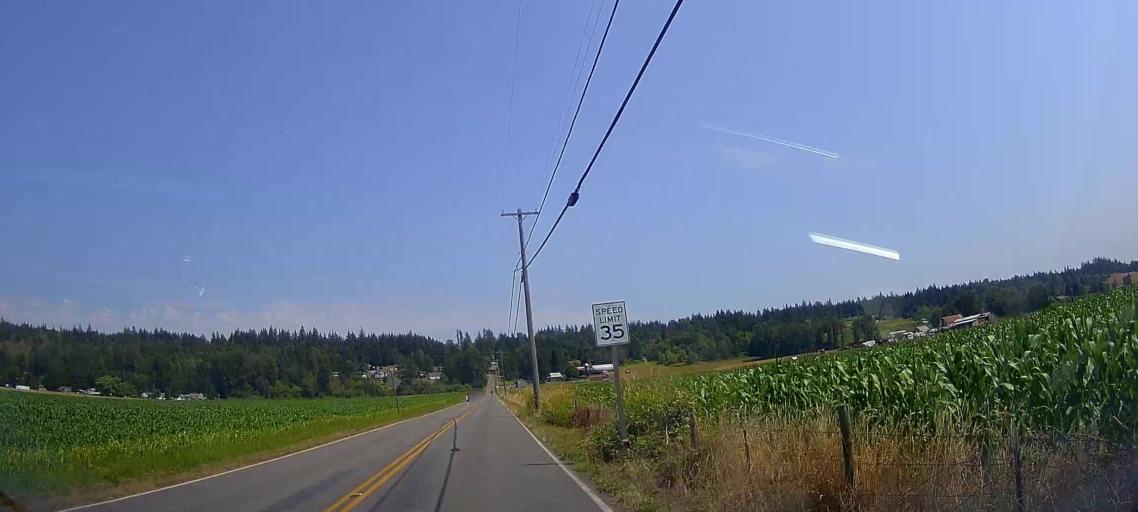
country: US
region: Washington
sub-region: Snohomish County
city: Sisco Heights
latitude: 48.0920
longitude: -122.1390
